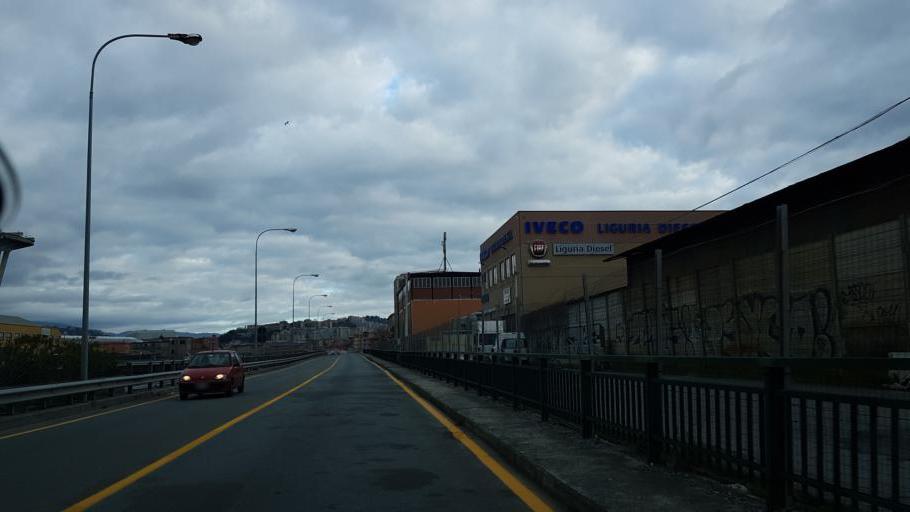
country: IT
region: Liguria
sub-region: Provincia di Genova
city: San Teodoro
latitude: 44.4240
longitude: 8.8872
